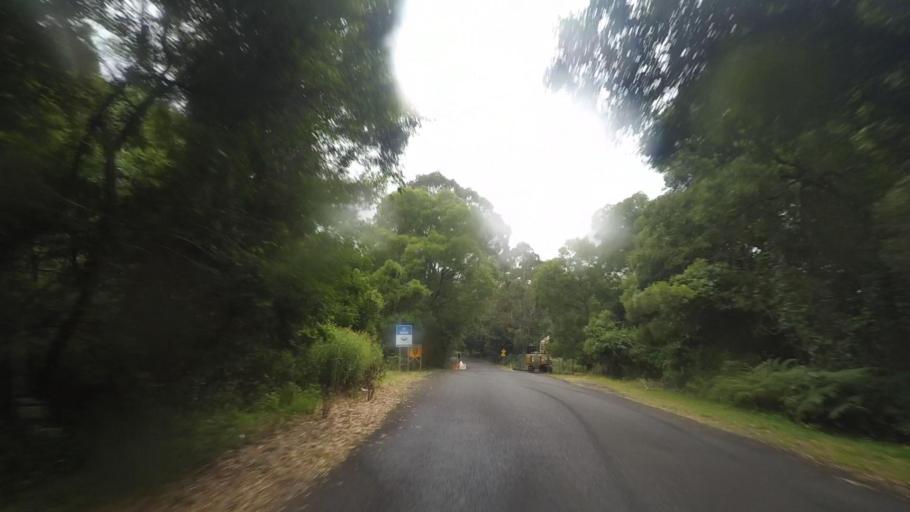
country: AU
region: New South Wales
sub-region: Wollongong
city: Cordeaux Heights
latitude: -34.4128
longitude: 150.8203
